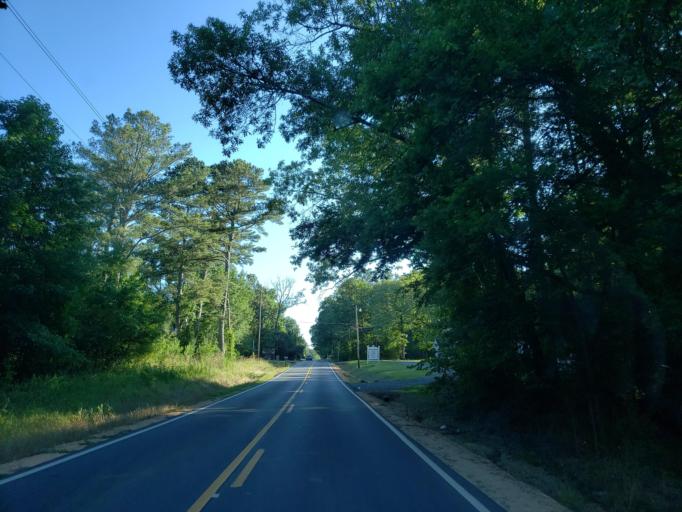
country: US
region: Georgia
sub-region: Floyd County
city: Shannon
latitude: 34.3394
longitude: -85.1534
